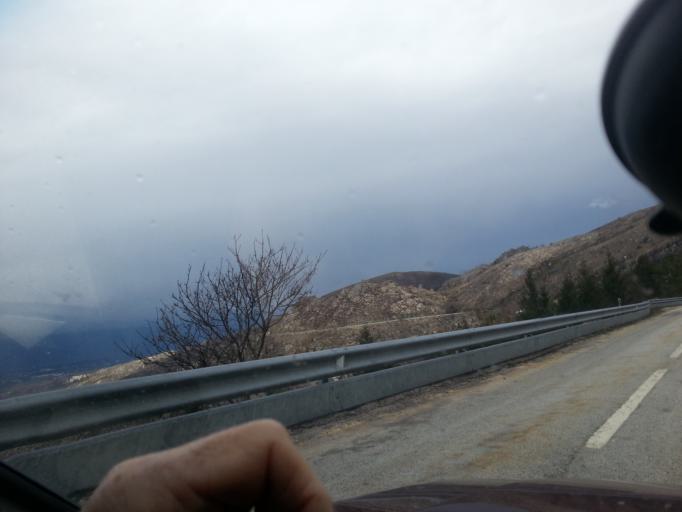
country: PT
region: Guarda
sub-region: Manteigas
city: Manteigas
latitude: 40.4295
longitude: -7.6072
